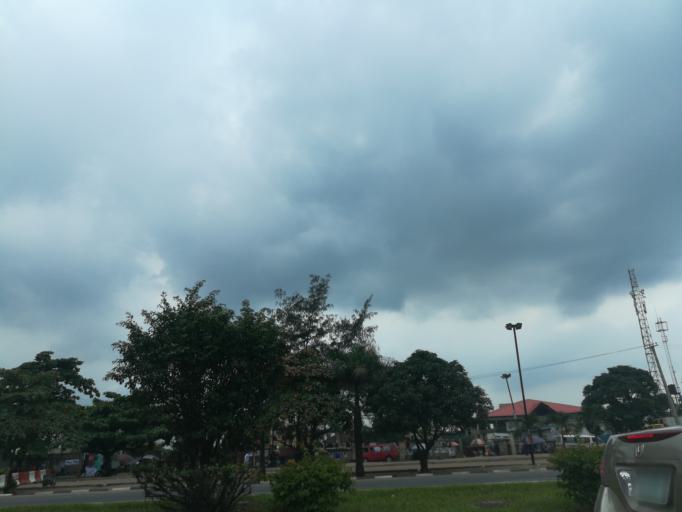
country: NG
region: Lagos
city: Ojota
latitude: 6.6003
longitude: 3.3776
